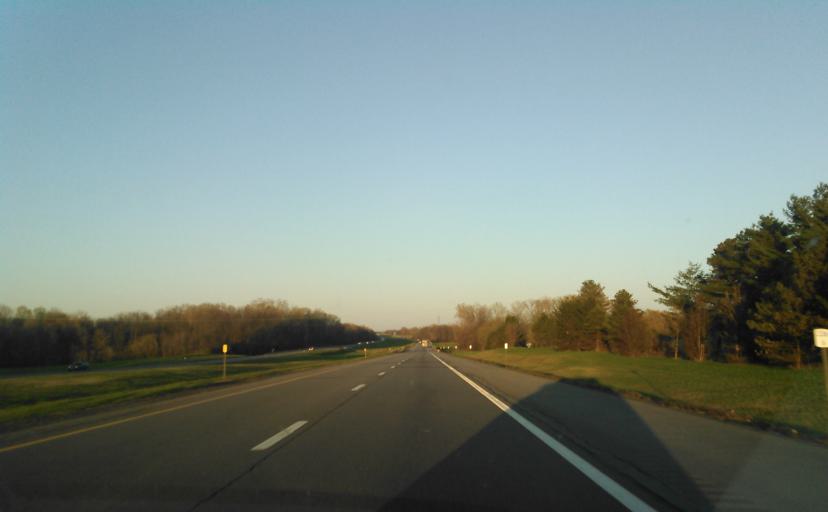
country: US
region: New York
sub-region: Ontario County
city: Clifton Springs
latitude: 42.9730
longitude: -77.1634
